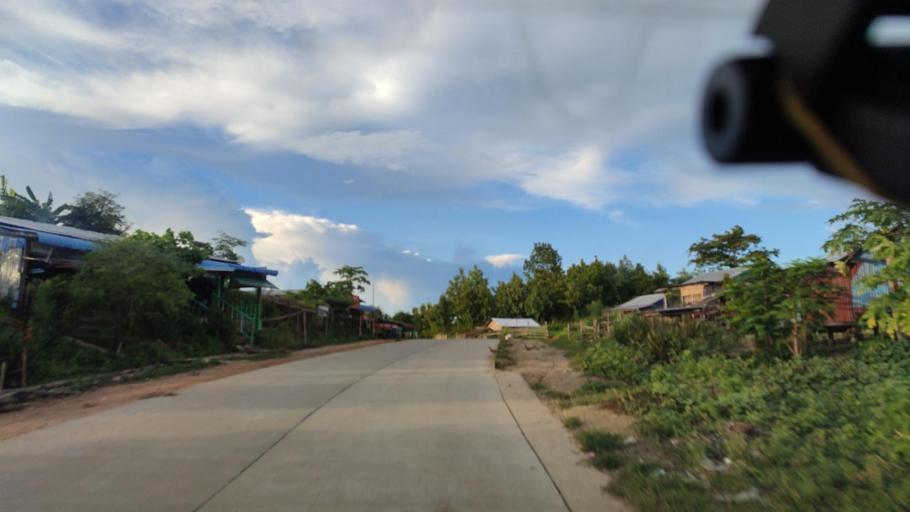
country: MM
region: Magway
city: Taungdwingyi
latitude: 20.0497
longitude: 95.7745
